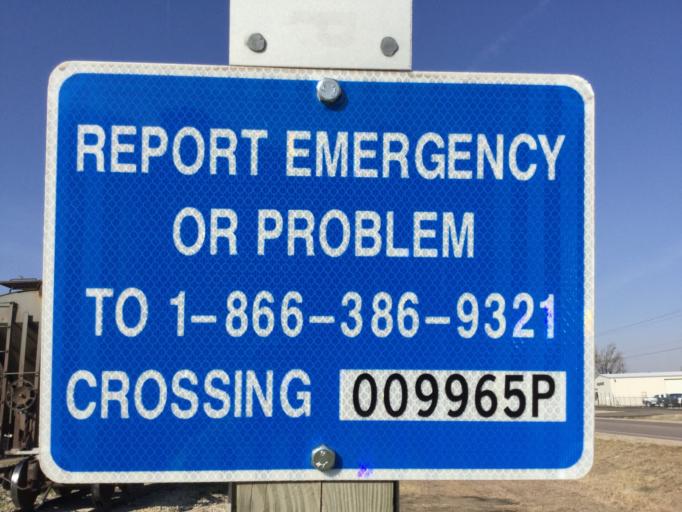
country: US
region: Kansas
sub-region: Barton County
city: Great Bend
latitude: 38.3528
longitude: -98.7838
